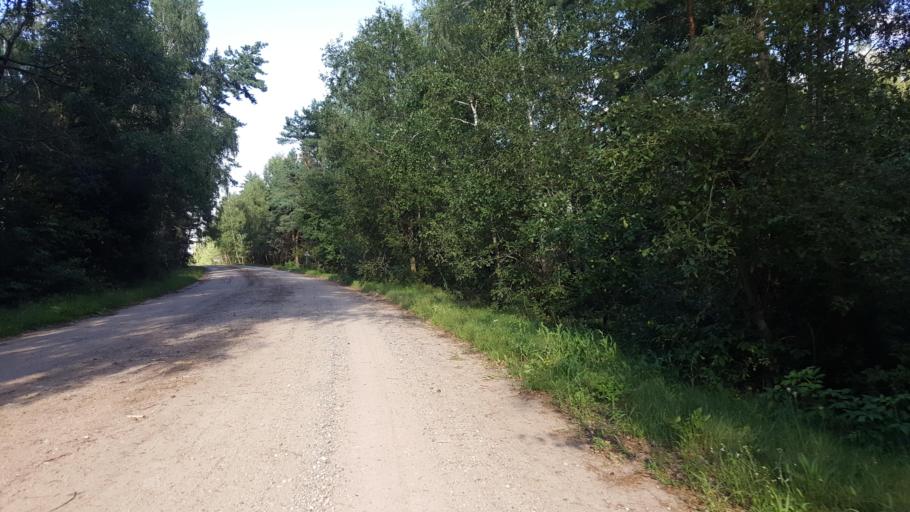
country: BY
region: Brest
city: Kamyanyets
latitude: 52.3639
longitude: 23.7218
